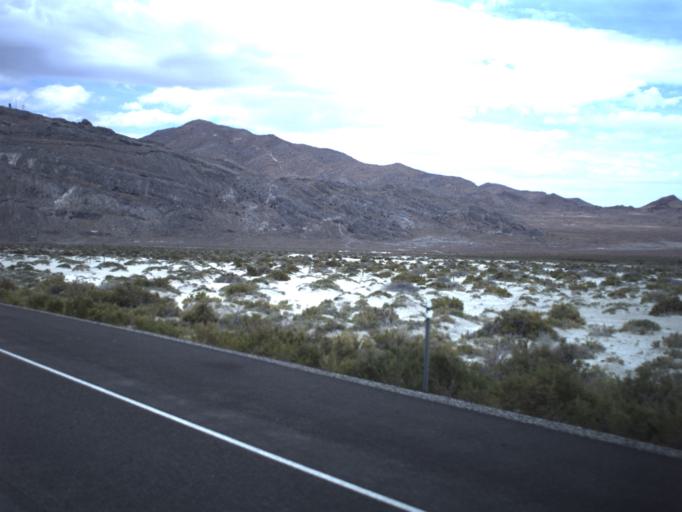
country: US
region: Utah
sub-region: Tooele County
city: Wendover
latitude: 40.7470
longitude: -114.0005
